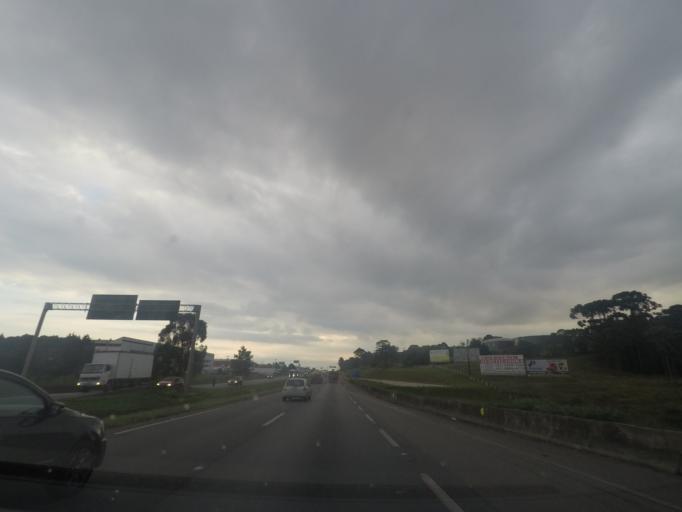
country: BR
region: Parana
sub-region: Sao Jose Dos Pinhais
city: Sao Jose dos Pinhais
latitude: -25.5699
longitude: -49.1875
